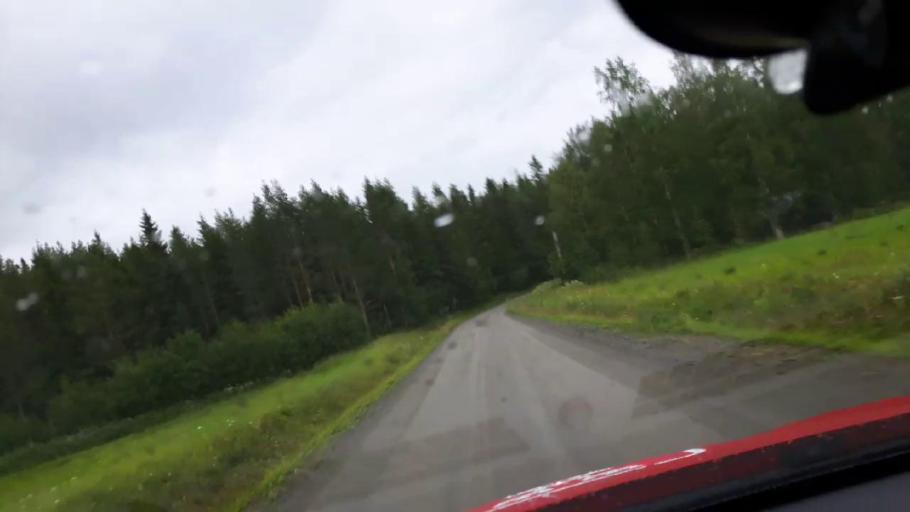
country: SE
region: Jaemtland
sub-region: OEstersunds Kommun
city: Brunflo
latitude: 62.9062
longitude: 14.8571
